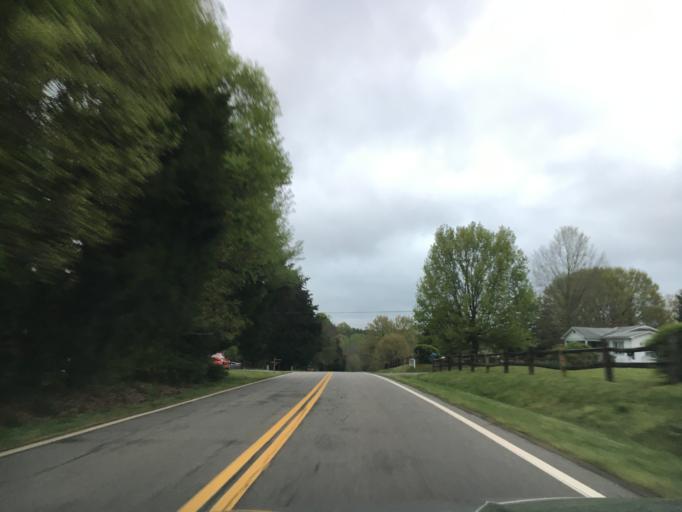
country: US
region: Virginia
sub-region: Halifax County
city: South Boston
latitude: 36.6523
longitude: -78.8732
